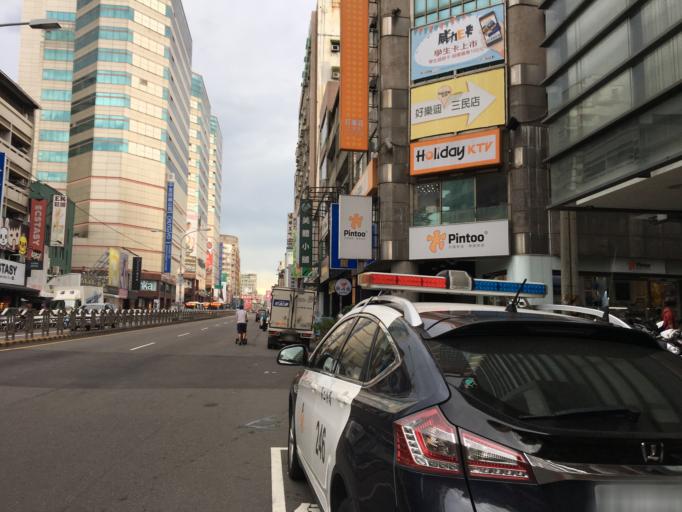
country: TW
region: Taiwan
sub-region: Taichung City
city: Taichung
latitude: 24.1506
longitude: 120.6845
